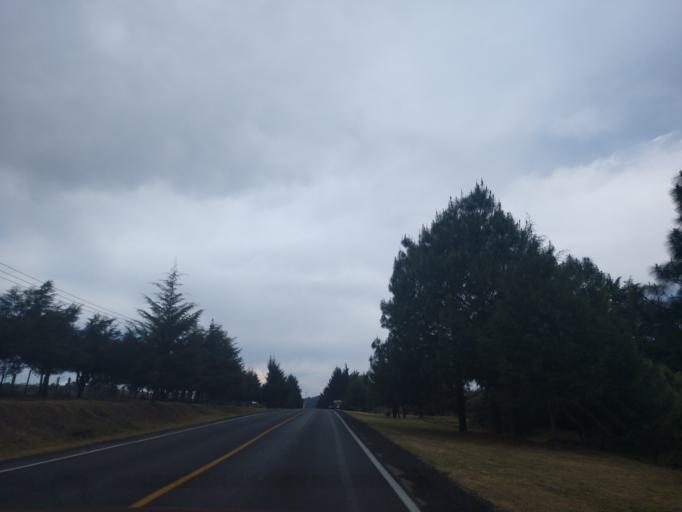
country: MX
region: Jalisco
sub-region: Mazamitla
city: Mazamitla
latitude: 19.9288
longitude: -103.0416
